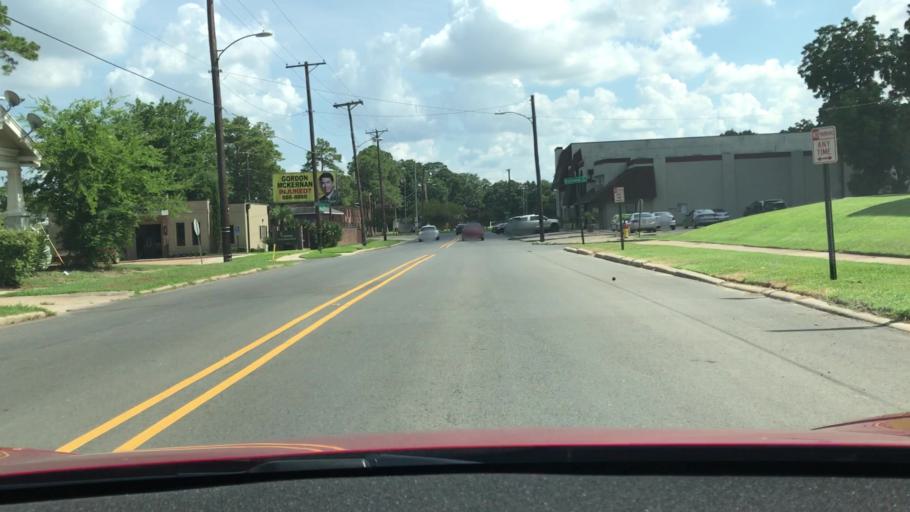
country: US
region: Louisiana
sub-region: Bossier Parish
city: Bossier City
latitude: 32.4871
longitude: -93.7332
